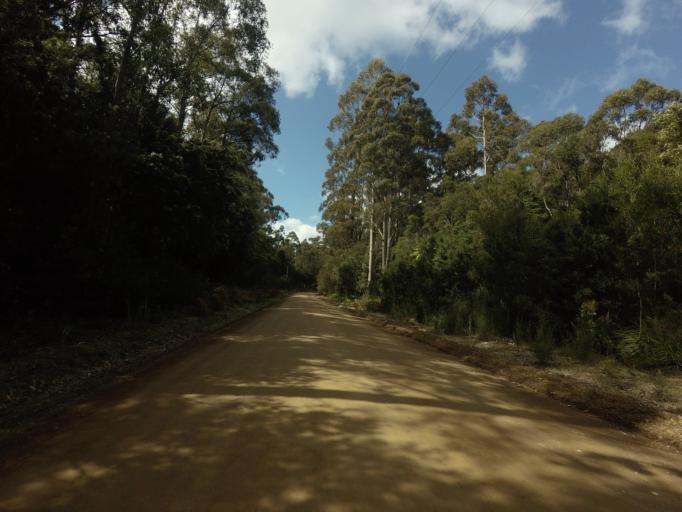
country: AU
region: Tasmania
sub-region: Huon Valley
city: Geeveston
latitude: -43.4131
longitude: 146.8975
